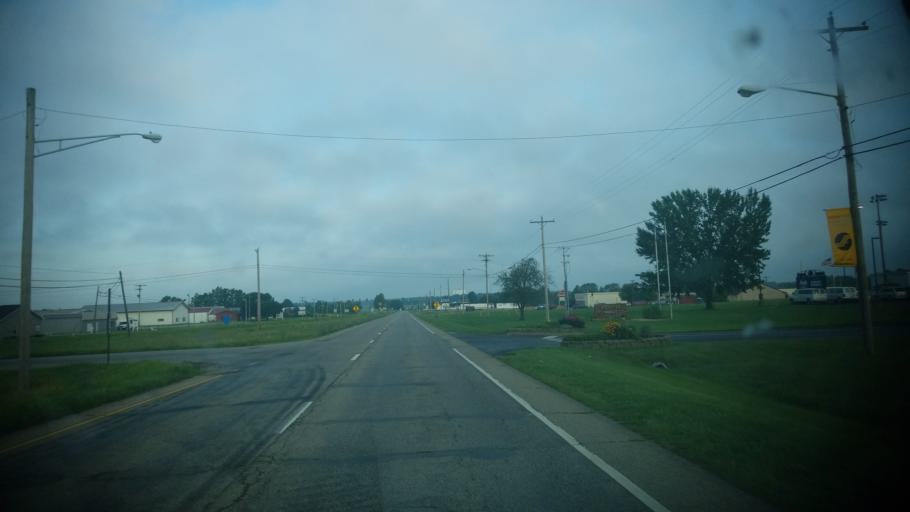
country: US
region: Illinois
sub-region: Wayne County
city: Fairfield
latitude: 38.3797
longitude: -88.3922
